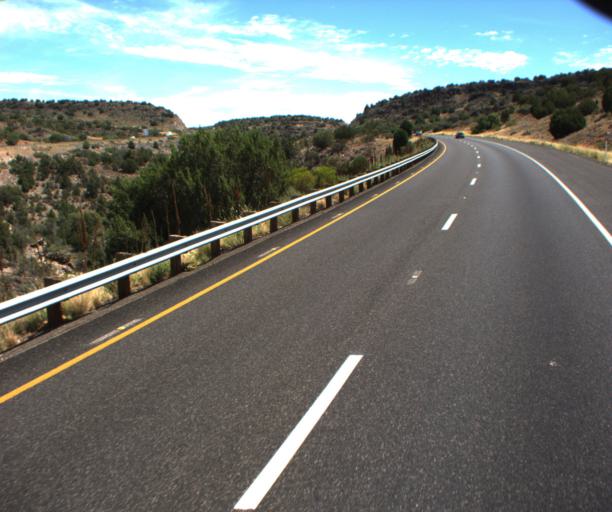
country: US
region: Arizona
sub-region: Yavapai County
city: Big Park
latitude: 34.7091
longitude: -111.7309
